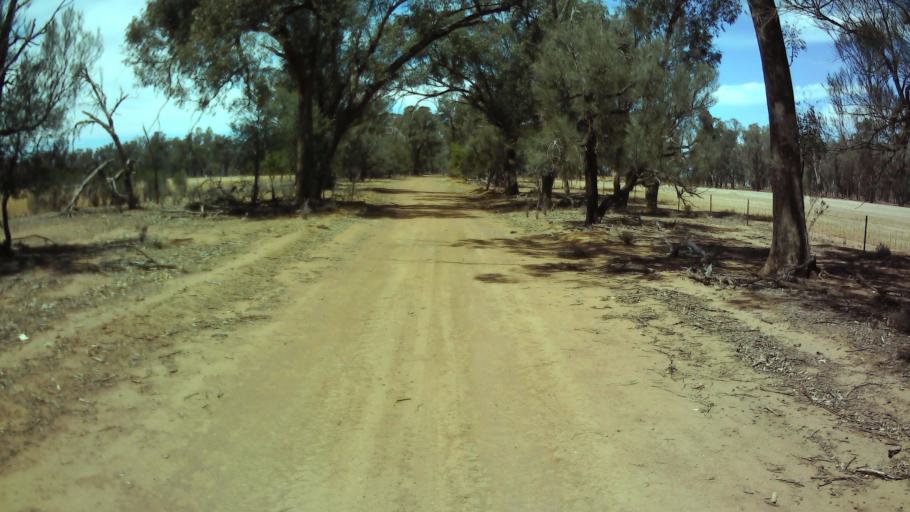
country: AU
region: New South Wales
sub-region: Weddin
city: Grenfell
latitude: -33.9086
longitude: 147.8069
